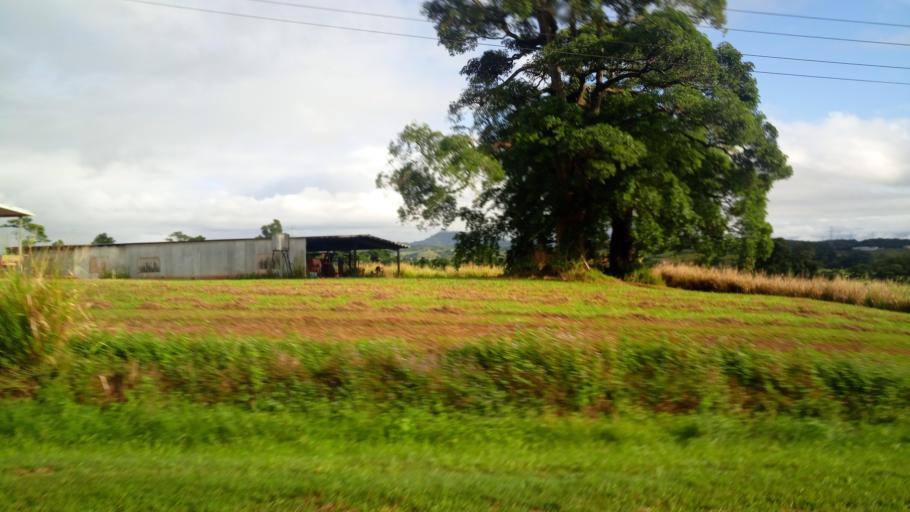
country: AU
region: Queensland
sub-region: Cassowary Coast
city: Innisfail
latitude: -17.5294
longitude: 145.9800
